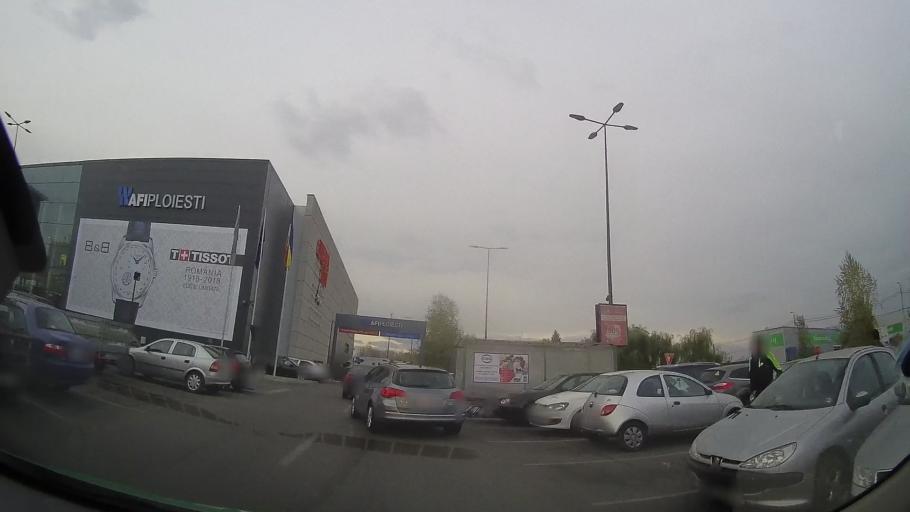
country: RO
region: Prahova
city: Ploiesti
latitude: 44.9468
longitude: 26.0342
